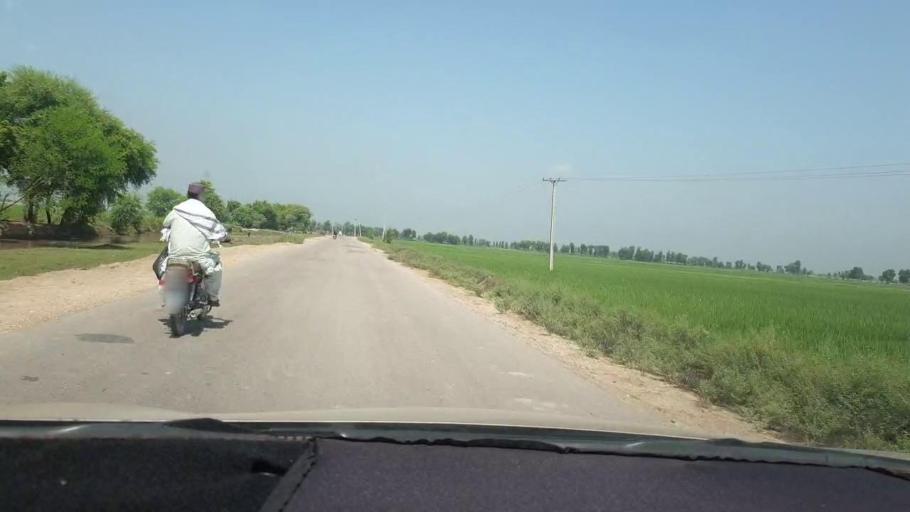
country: PK
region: Sindh
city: Miro Khan
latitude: 27.7661
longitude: 68.0716
